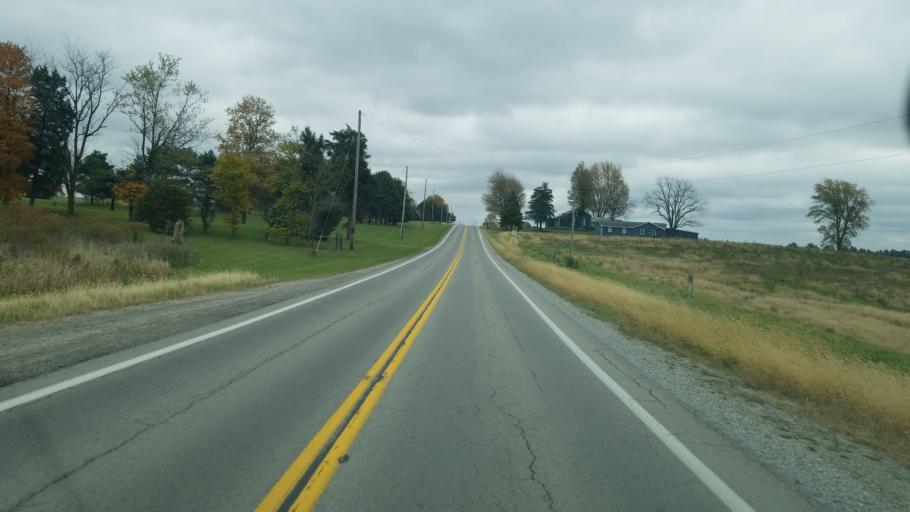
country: US
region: Ohio
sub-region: Sandusky County
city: Mount Carmel
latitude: 41.0811
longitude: -82.9565
